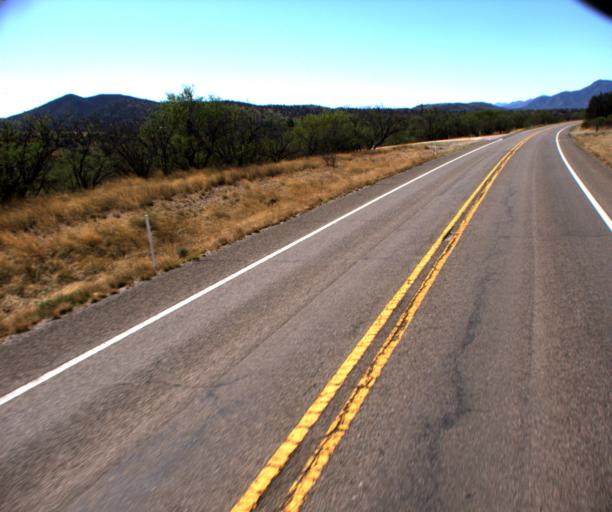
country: US
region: Arizona
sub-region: Santa Cruz County
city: Rio Rico
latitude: 31.6359
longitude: -110.7133
